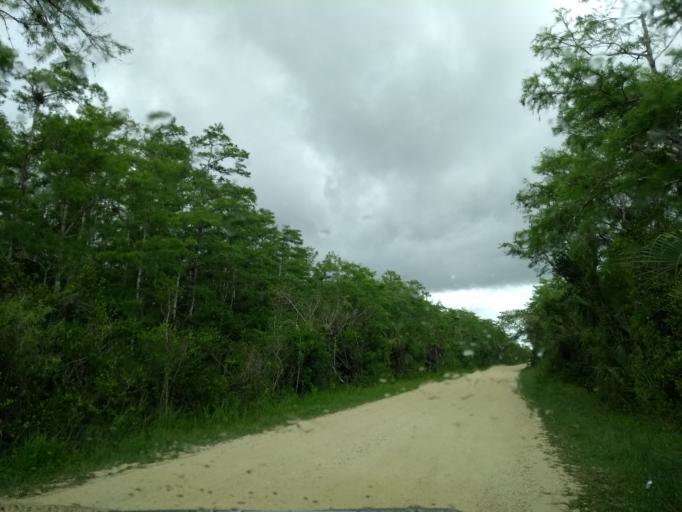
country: US
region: Florida
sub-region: Miami-Dade County
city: The Hammocks
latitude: 25.7467
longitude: -80.9542
